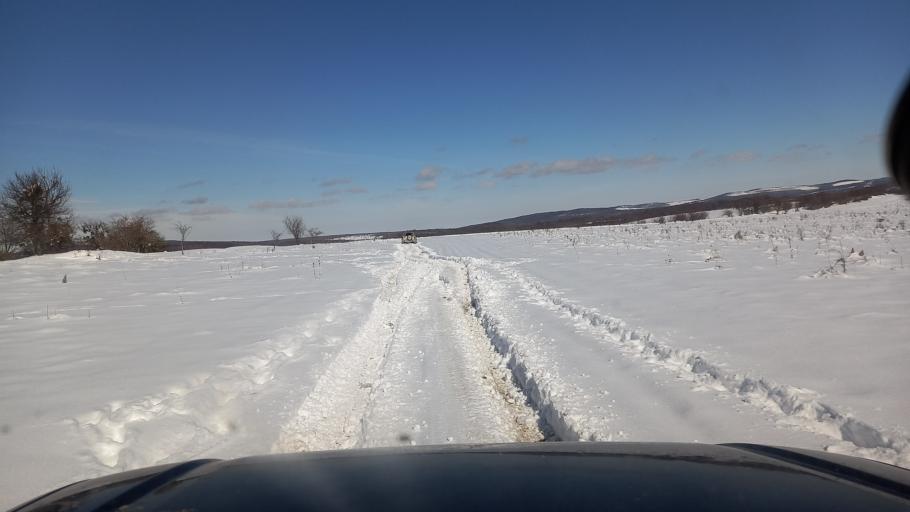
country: RU
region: Krasnodarskiy
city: Gubskaya
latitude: 44.3366
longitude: 40.4283
